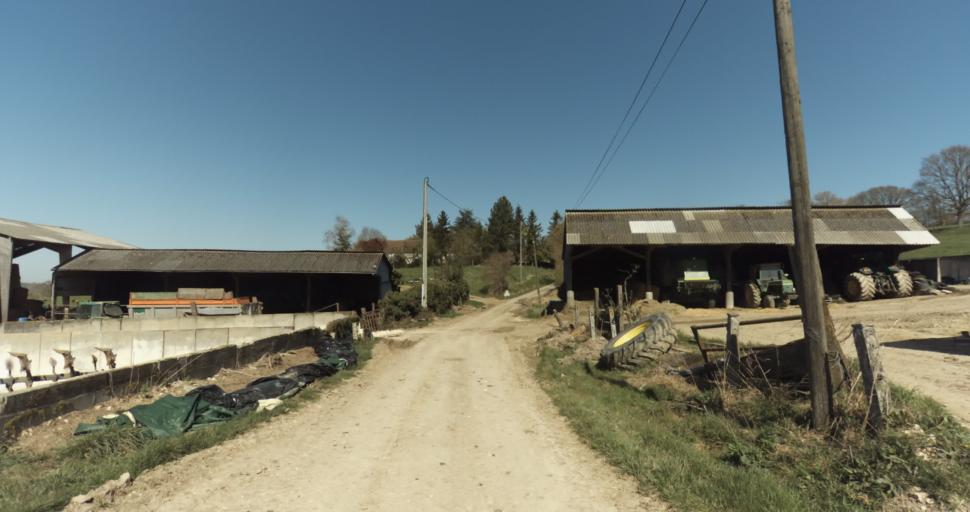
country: FR
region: Lower Normandy
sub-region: Departement du Calvados
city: Saint-Pierre-sur-Dives
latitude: 48.9926
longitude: 0.0360
